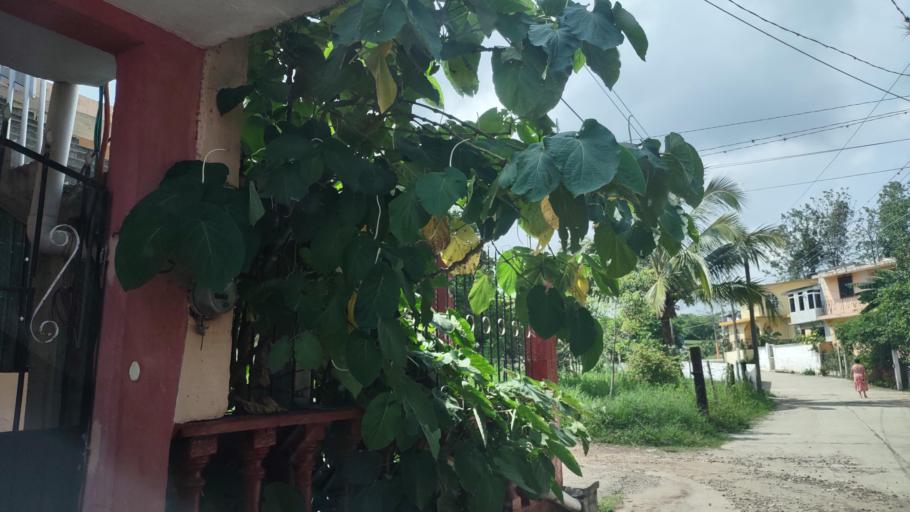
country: MX
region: Veracruz
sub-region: Emiliano Zapata
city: Jacarandas
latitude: 19.4698
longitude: -96.8364
